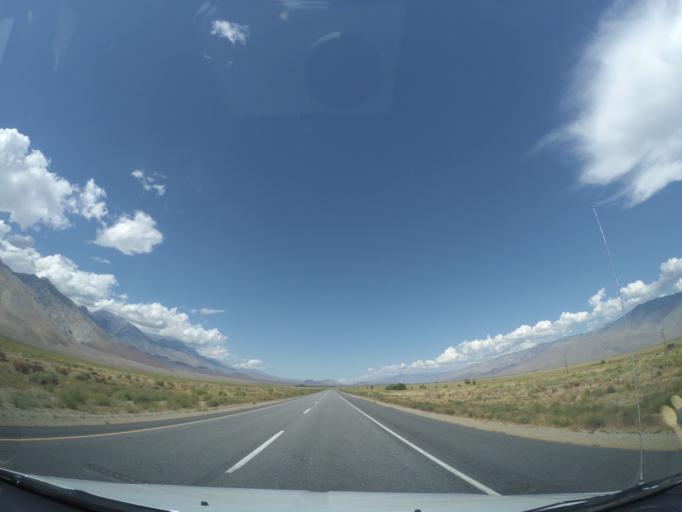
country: US
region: California
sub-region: Inyo County
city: Big Pine
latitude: 36.8866
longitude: -118.2408
